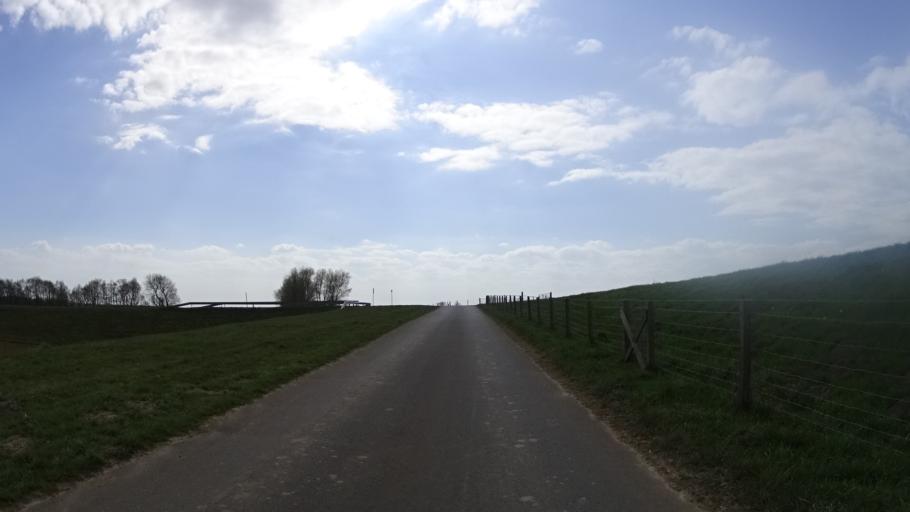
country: DE
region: Lower Saxony
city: Rhede
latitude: 53.0948
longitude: 7.2985
